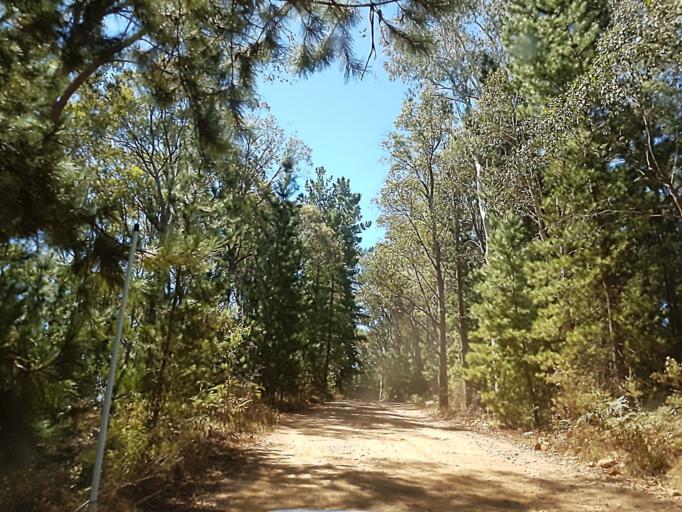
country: AU
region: Victoria
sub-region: Alpine
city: Mount Beauty
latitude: -36.7606
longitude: 146.9624
